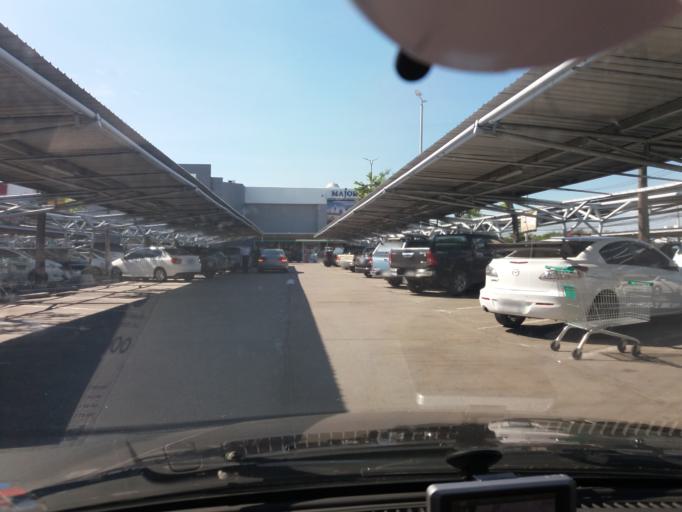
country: TH
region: Suphan Buri
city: Suphan Buri
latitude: 14.4699
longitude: 100.1306
